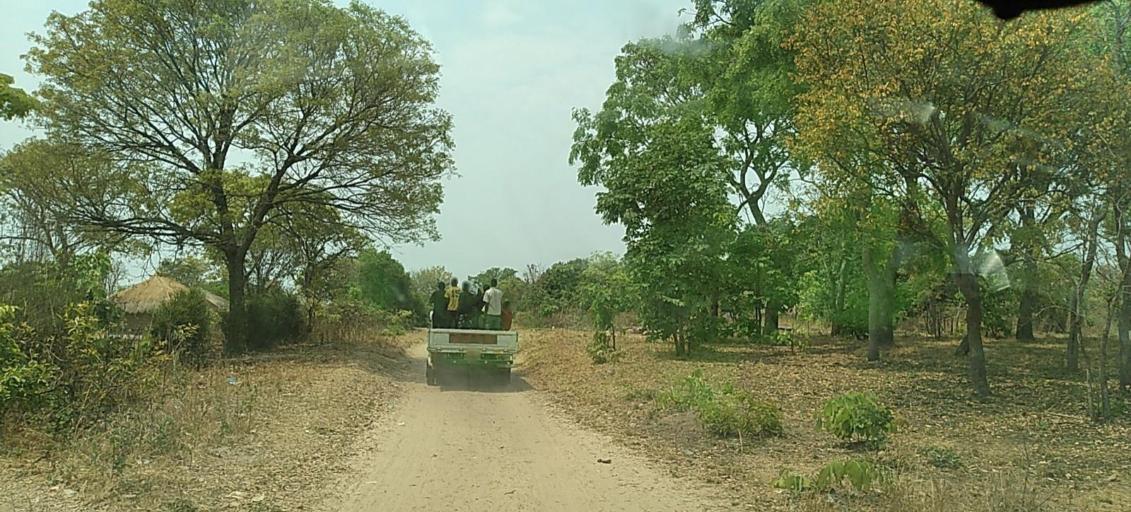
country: ZM
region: North-Western
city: Kabompo
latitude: -13.4846
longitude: 24.4607
